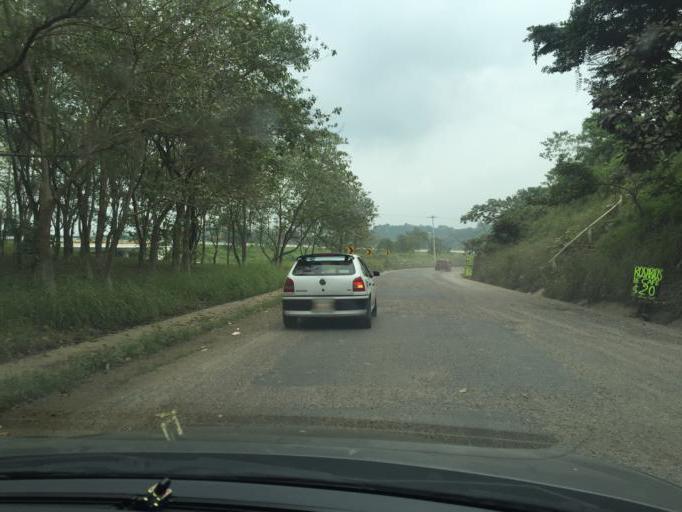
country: MX
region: Veracruz
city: Villa Nanchital
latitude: 18.0730
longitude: -94.3195
